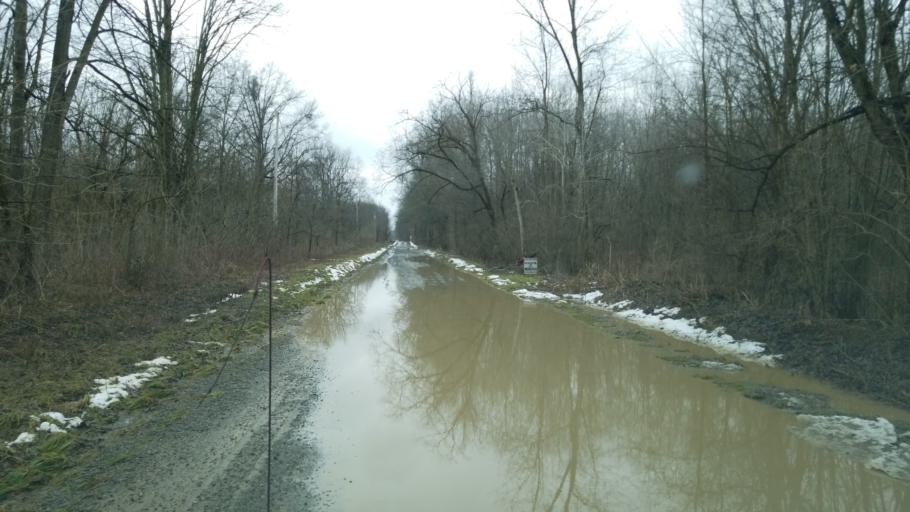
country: US
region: Ohio
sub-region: Ashtabula County
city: Orwell
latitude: 41.4378
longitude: -80.9350
